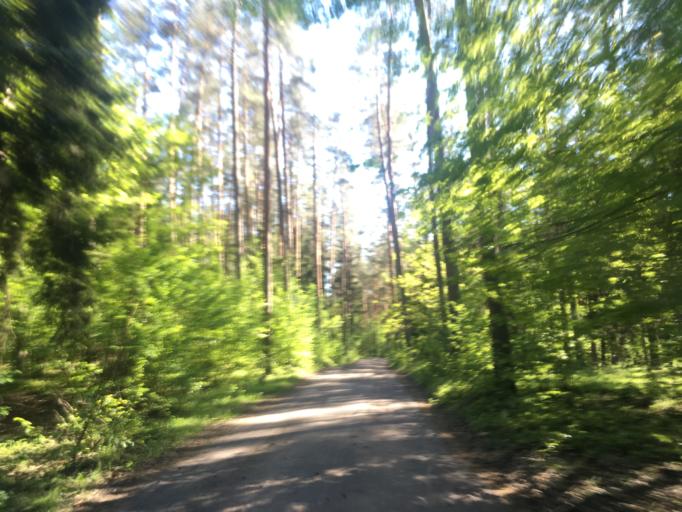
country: PL
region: Warmian-Masurian Voivodeship
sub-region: Powiat mragowski
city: Mikolajki
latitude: 53.7467
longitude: 21.6129
